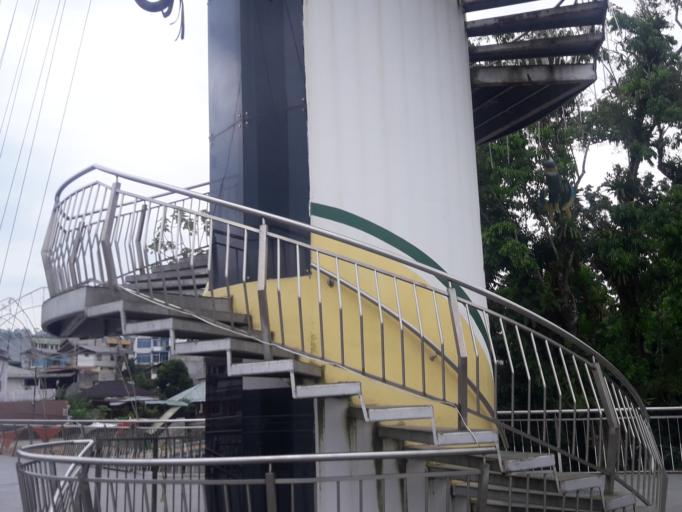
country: EC
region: Napo
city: Tena
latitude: -0.9930
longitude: -77.8157
